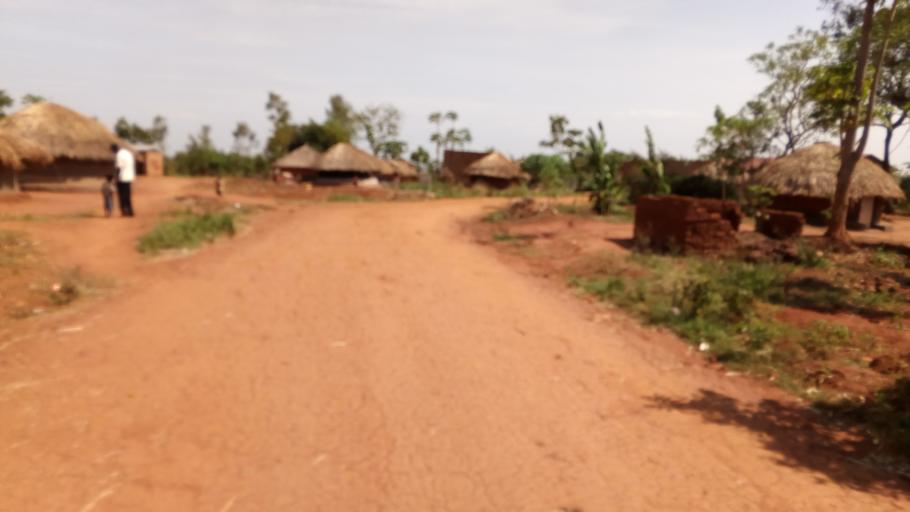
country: UG
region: Northern Region
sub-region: Gulu District
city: Gulu
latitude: 2.7908
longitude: 32.3202
